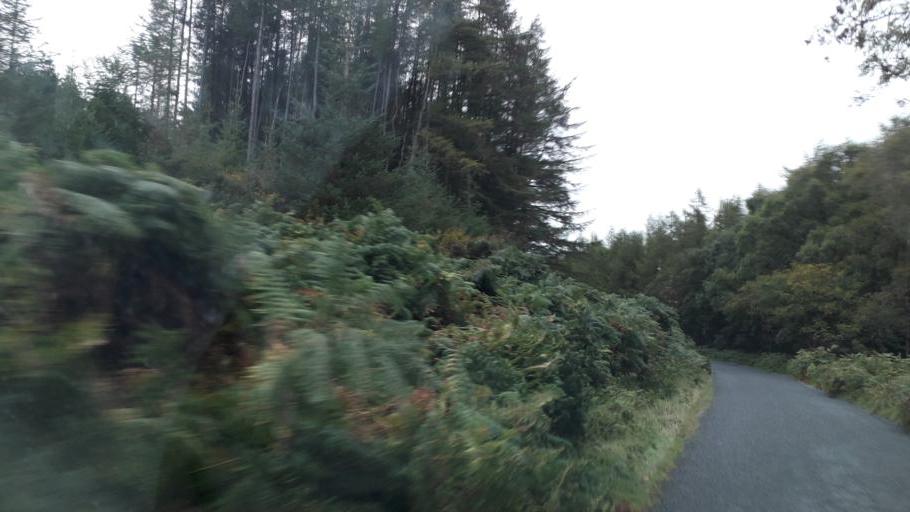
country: IE
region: Leinster
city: Ballinteer
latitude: 53.1863
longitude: -6.2851
